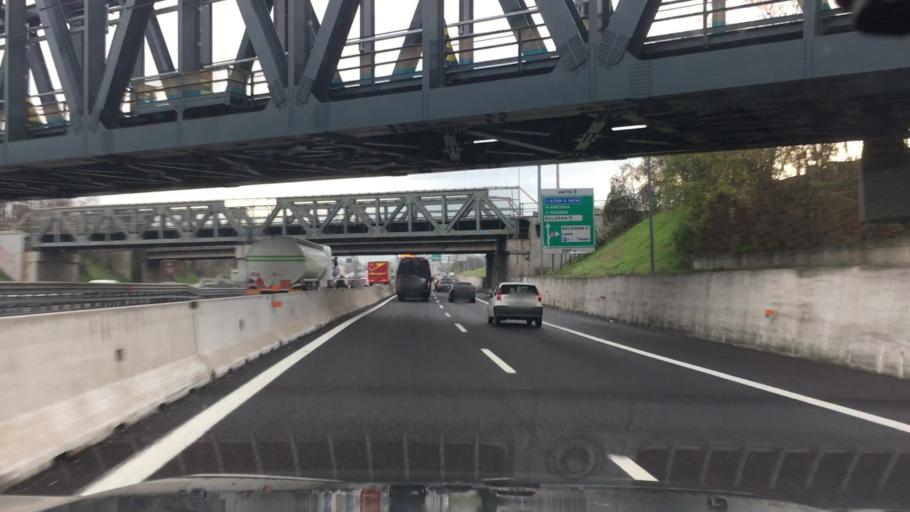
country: IT
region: Emilia-Romagna
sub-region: Provincia di Bologna
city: Trebbo
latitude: 44.5319
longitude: 11.3339
